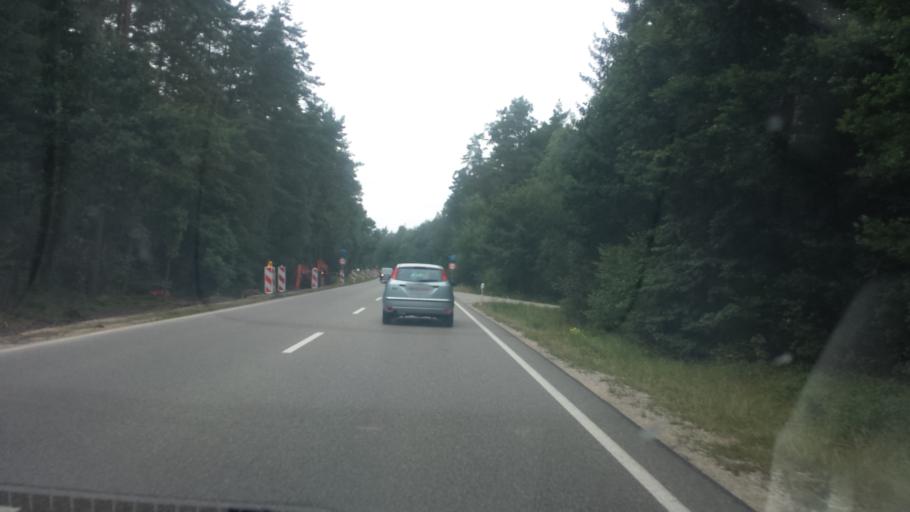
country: DE
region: Bavaria
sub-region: Regierungsbezirk Mittelfranken
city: Heilsbronn
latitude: 49.3205
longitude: 10.7908
